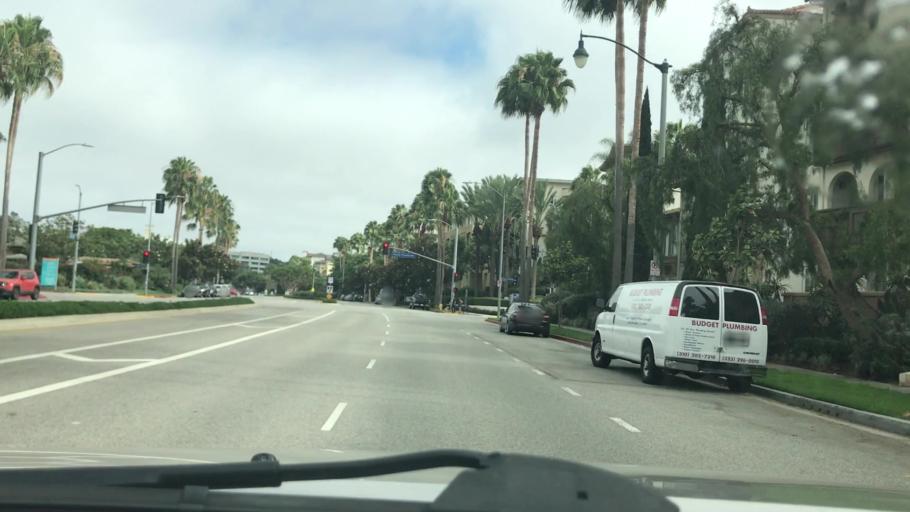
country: US
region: California
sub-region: Los Angeles County
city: Marina del Rey
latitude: 33.9720
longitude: -118.4272
